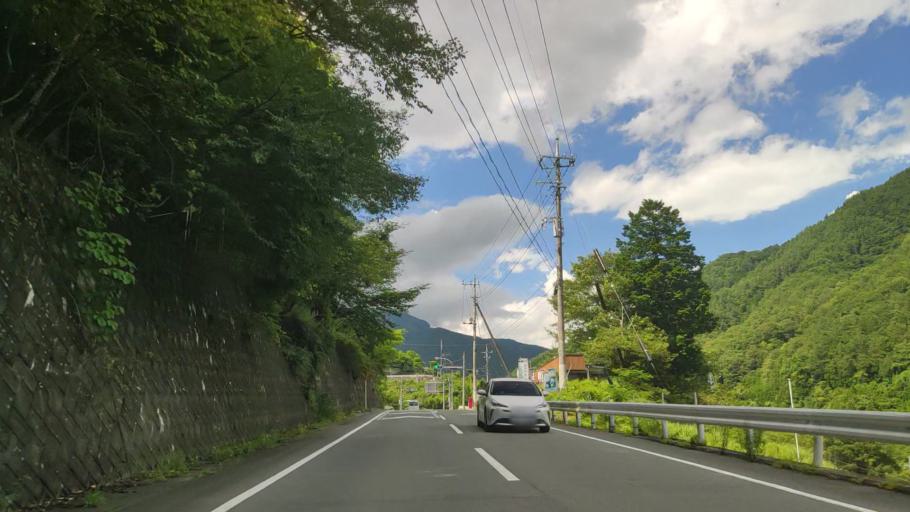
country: JP
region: Yamanashi
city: Enzan
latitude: 35.7769
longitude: 138.7387
